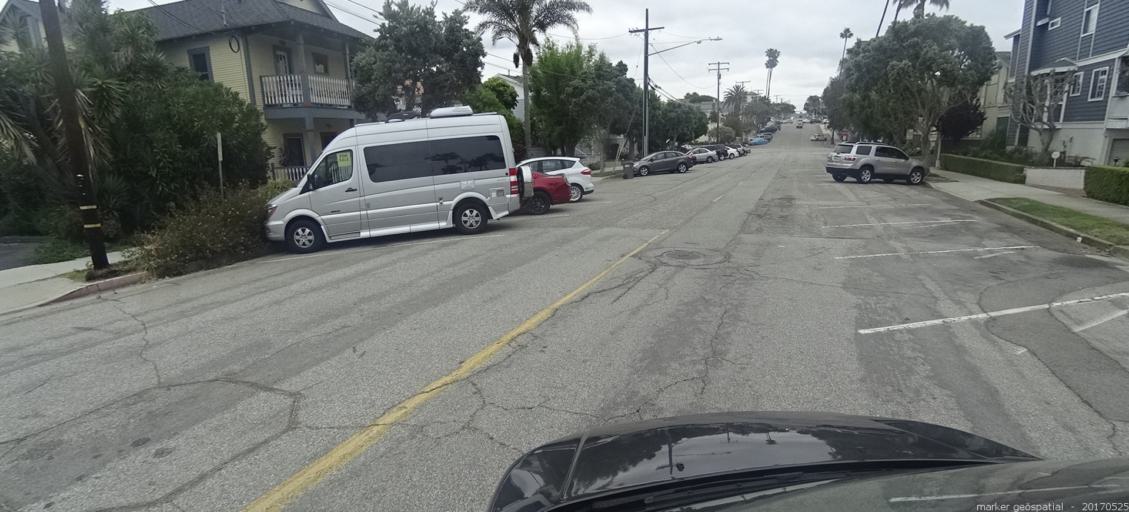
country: US
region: California
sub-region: Los Angeles County
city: Redondo Beach
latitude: 33.8419
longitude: -118.3883
